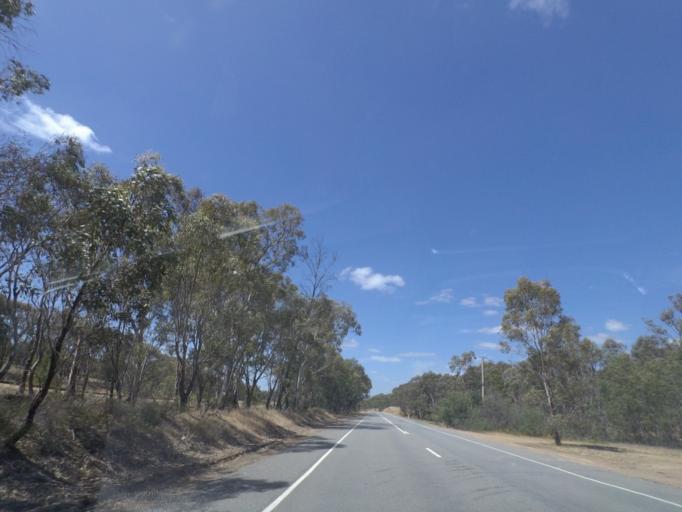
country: AU
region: Victoria
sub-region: Wangaratta
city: Wangaratta
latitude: -36.4619
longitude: 146.2300
